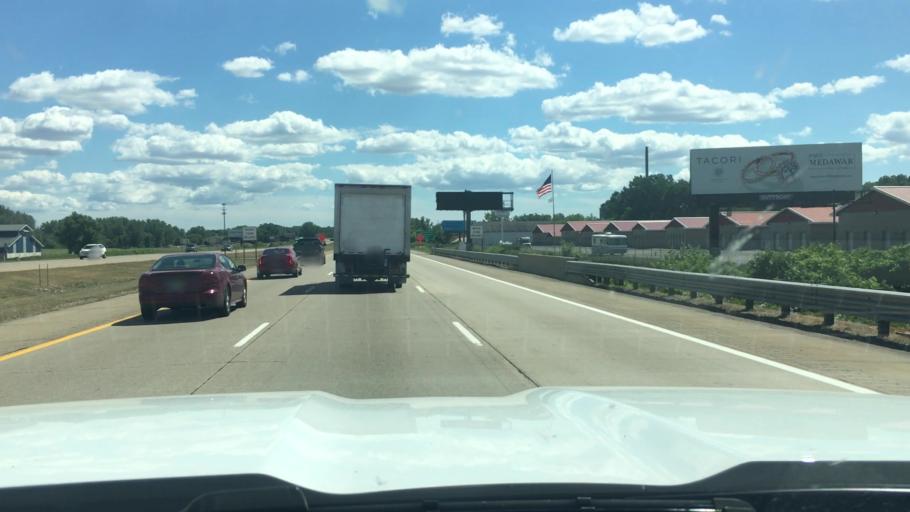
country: US
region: Michigan
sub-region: Kent County
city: Comstock Park
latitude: 43.0330
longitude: -85.6632
